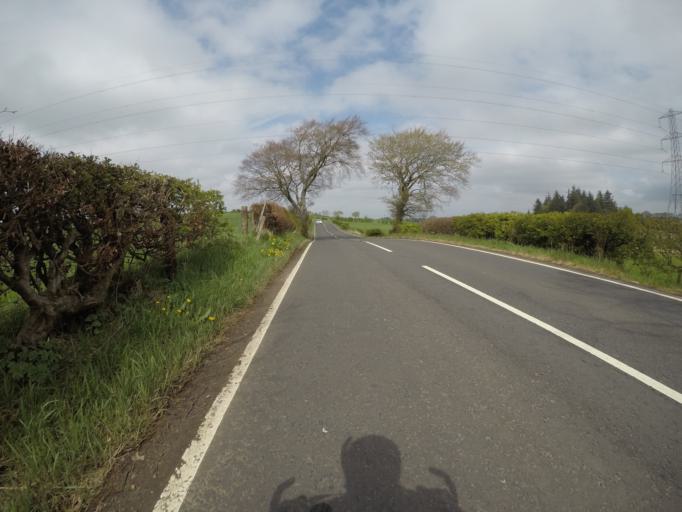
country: GB
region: Scotland
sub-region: East Renfrewshire
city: Barrhead
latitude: 55.7660
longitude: -4.3747
